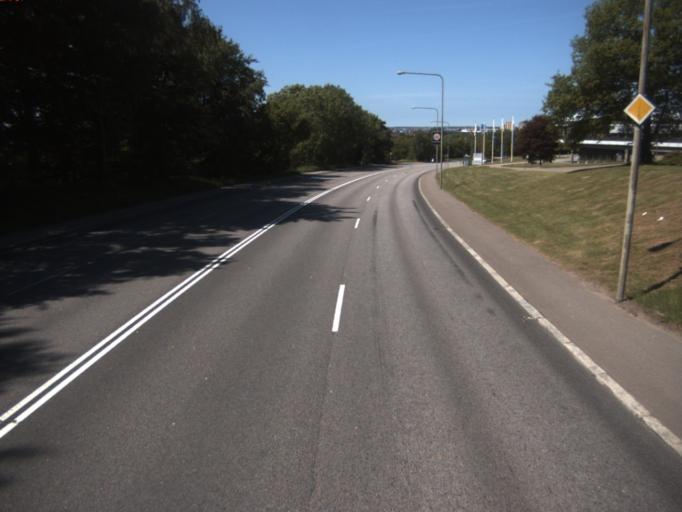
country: SE
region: Skane
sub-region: Helsingborg
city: Rydeback
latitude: 56.0146
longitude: 12.7431
